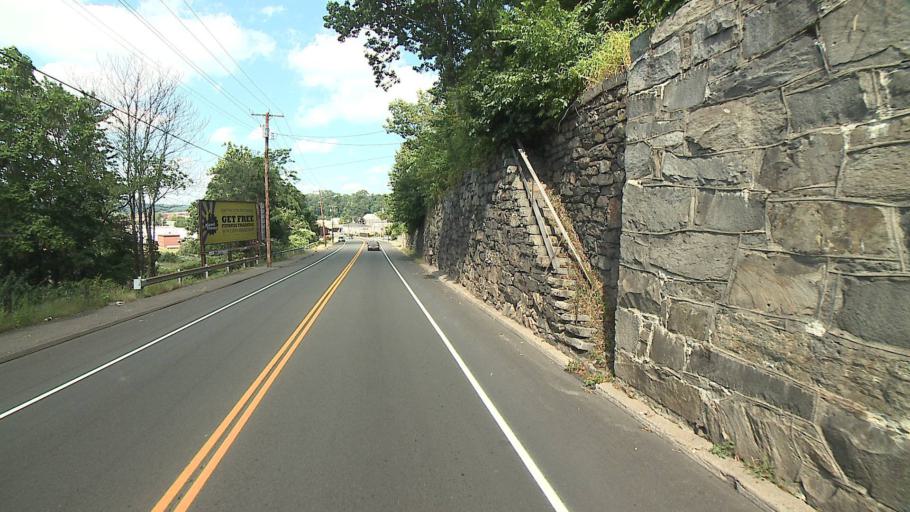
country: US
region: Connecticut
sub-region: New Haven County
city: Ansonia
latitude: 41.3336
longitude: -73.0764
